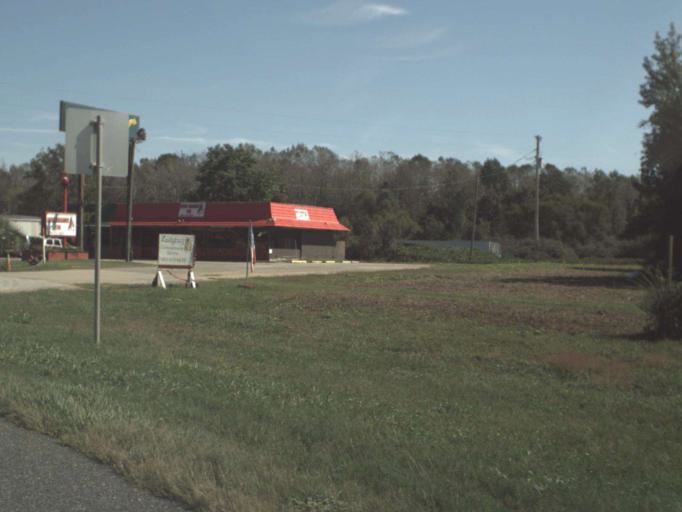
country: US
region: Florida
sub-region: Jackson County
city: Marianna
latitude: 30.7603
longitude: -85.3784
